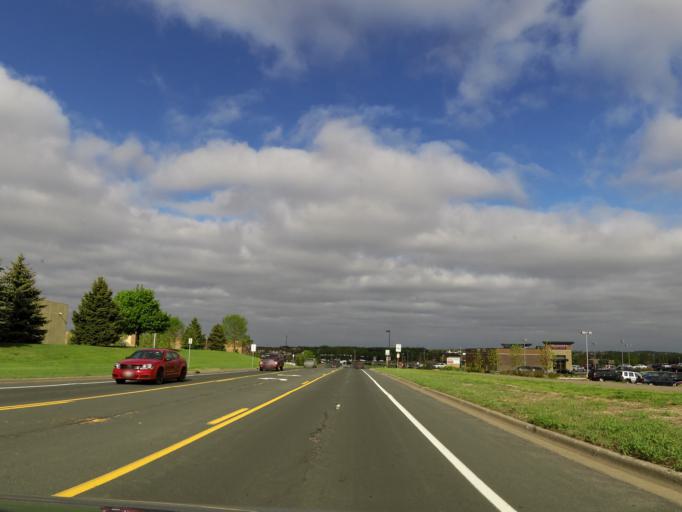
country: US
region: Minnesota
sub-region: Washington County
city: Woodbury
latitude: 44.9415
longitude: -92.9103
